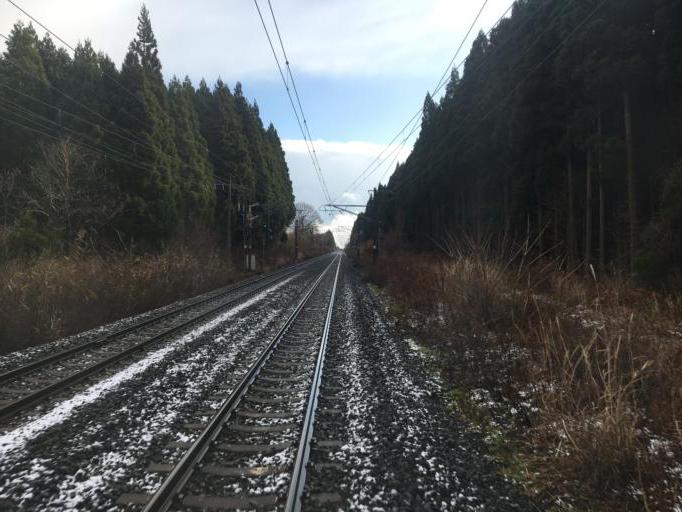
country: JP
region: Aomori
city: Aomori Shi
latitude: 40.9122
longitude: 141.0447
